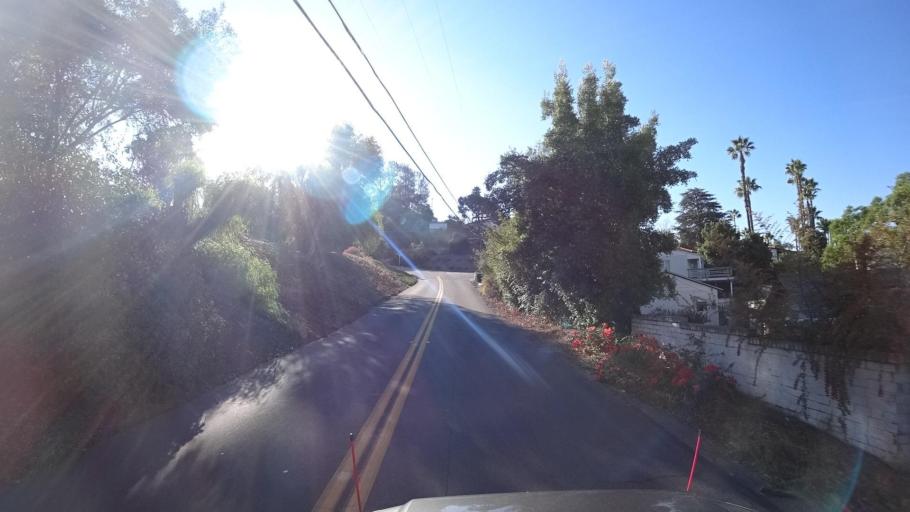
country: US
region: California
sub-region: San Diego County
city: Casa de Oro-Mount Helix
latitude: 32.7763
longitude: -116.9949
